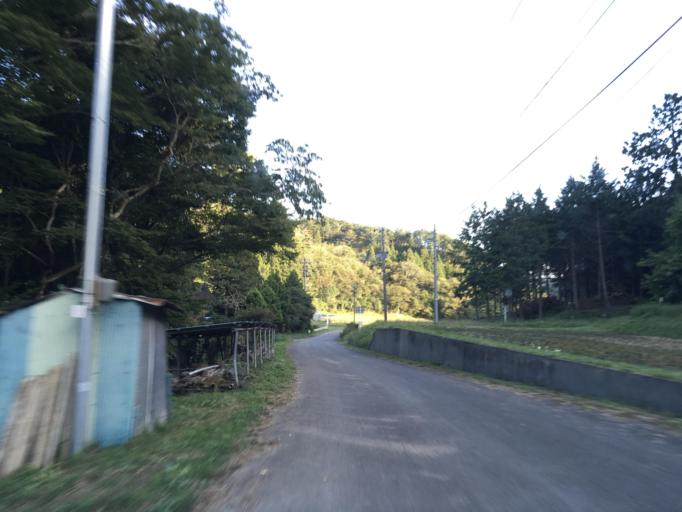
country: JP
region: Iwate
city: Ichinoseki
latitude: 38.7963
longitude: 141.4199
